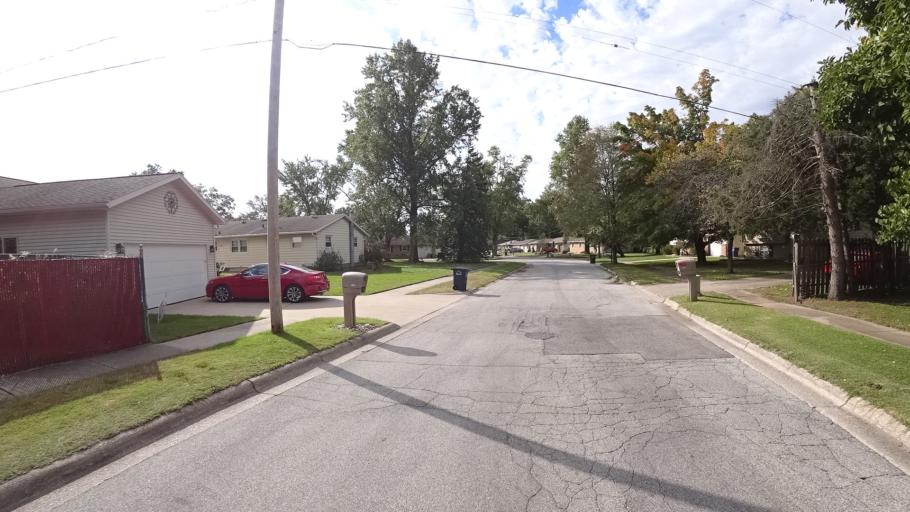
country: US
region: Indiana
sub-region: LaPorte County
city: Trail Creek
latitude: 41.7017
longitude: -86.8663
